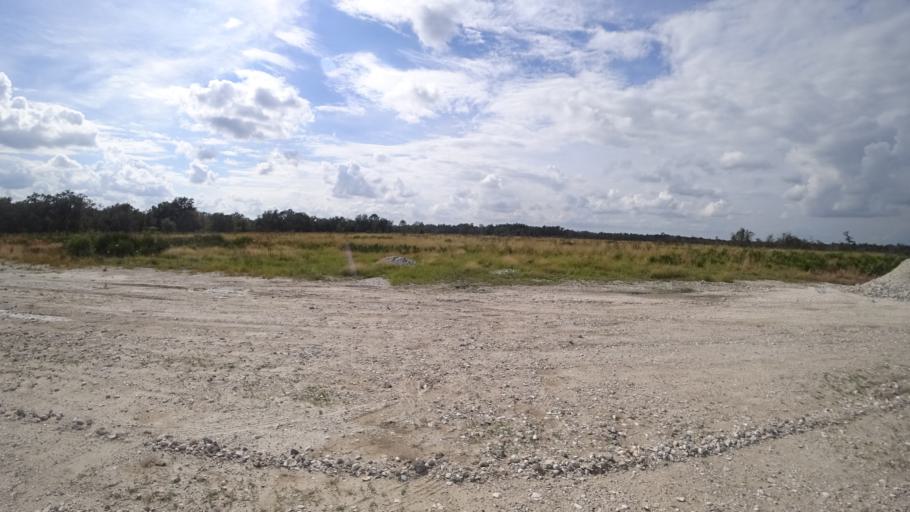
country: US
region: Florida
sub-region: Hillsborough County
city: Wimauma
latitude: 27.5255
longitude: -82.1275
